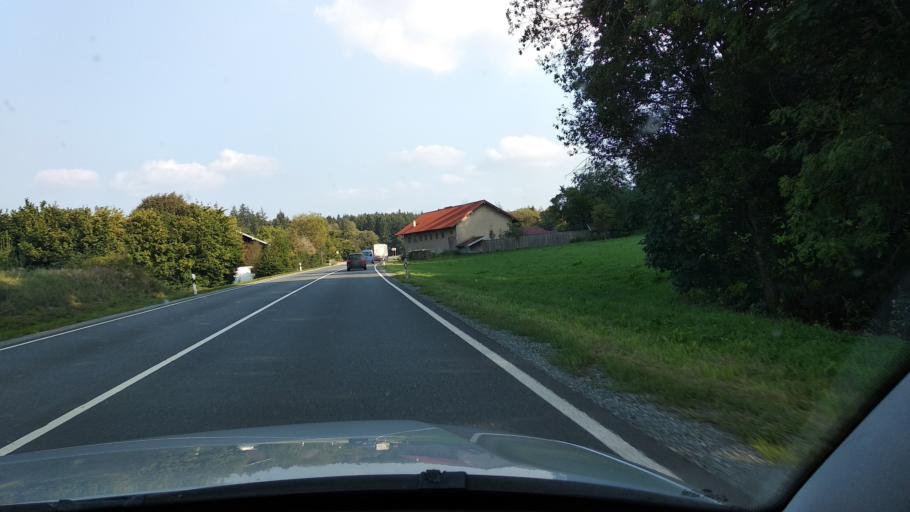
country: DE
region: Bavaria
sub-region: Upper Bavaria
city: Babensham
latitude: 48.0482
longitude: 12.2864
